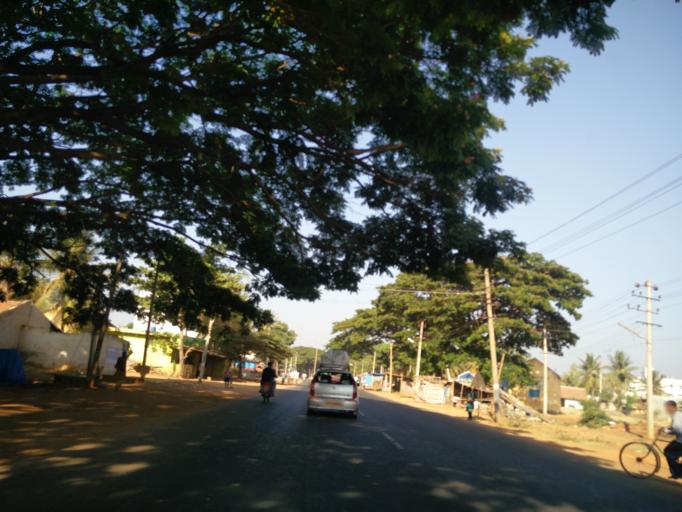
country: IN
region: Karnataka
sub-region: Tumkur
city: Gubbi
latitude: 13.3100
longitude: 76.9504
